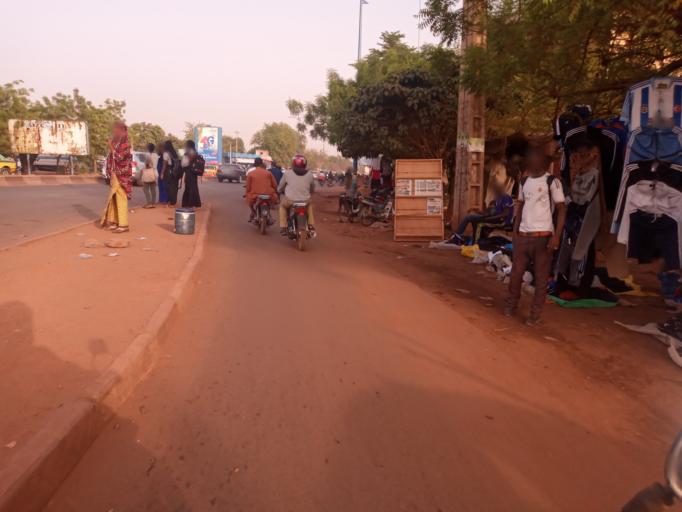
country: ML
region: Bamako
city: Bamako
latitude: 12.6062
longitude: -7.9724
